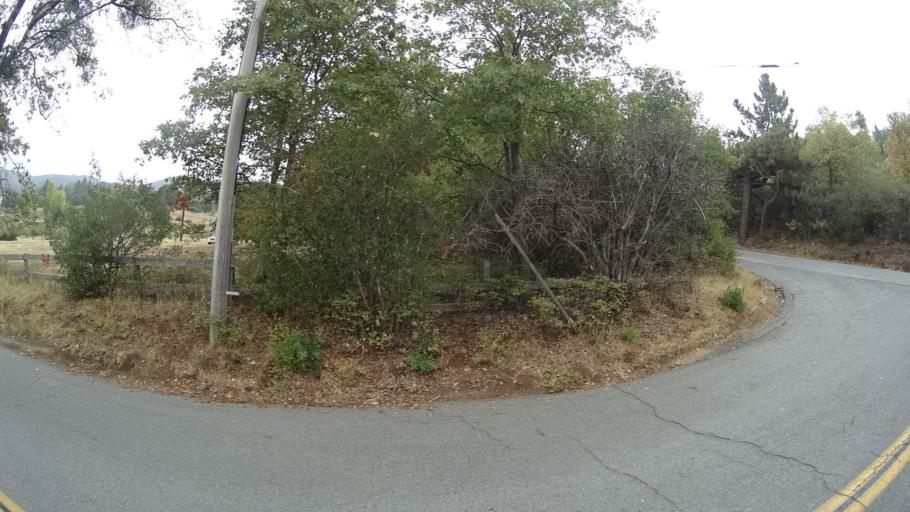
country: US
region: California
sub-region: San Diego County
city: Julian
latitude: 33.0428
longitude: -116.6012
